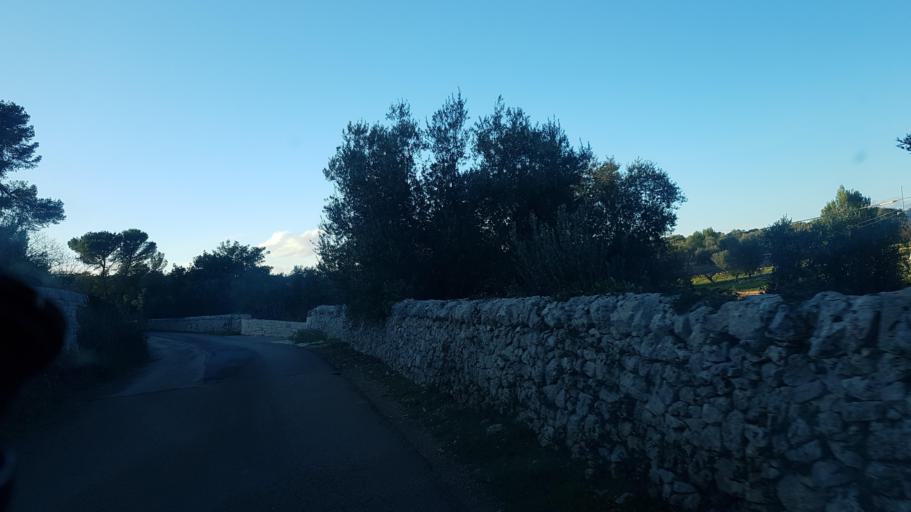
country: IT
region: Apulia
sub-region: Provincia di Brindisi
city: Ostuni
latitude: 40.7030
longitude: 17.5403
